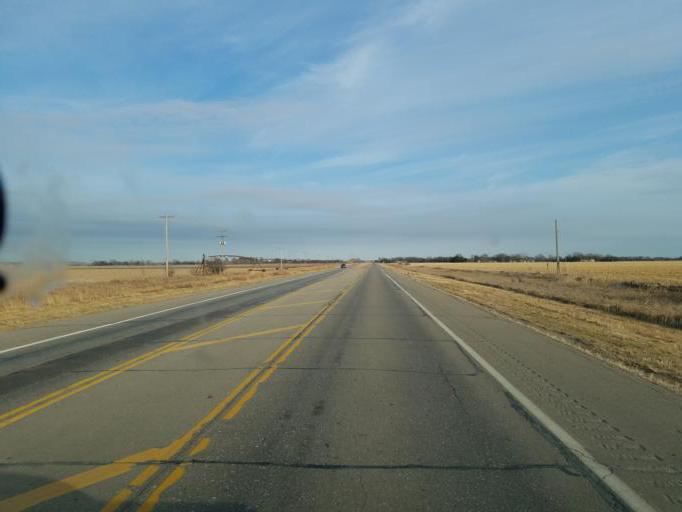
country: US
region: South Dakota
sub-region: Union County
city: Dakota Dunes
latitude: 42.4483
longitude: -96.5478
